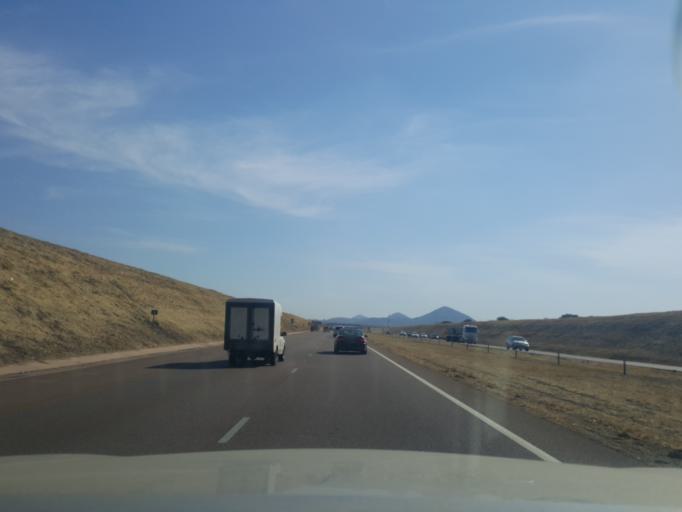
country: ZA
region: Gauteng
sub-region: City of Tshwane Metropolitan Municipality
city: Pretoria
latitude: -25.6398
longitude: 28.2148
